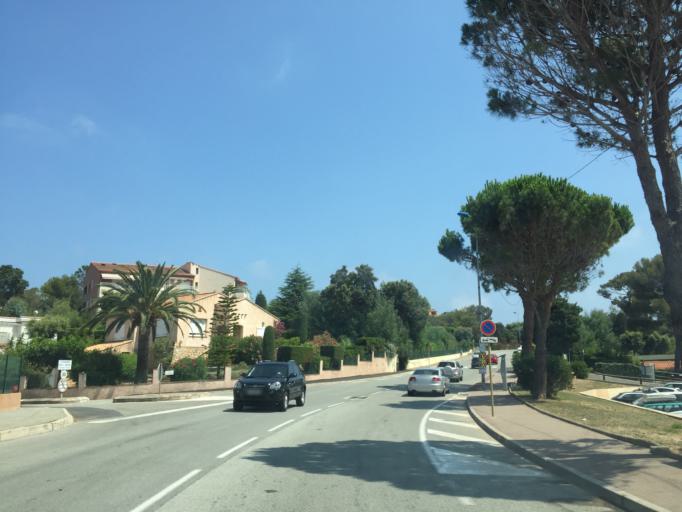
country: FR
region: Provence-Alpes-Cote d'Azur
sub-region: Departement du Var
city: Saint-Raphael
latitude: 43.4339
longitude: 6.8670
